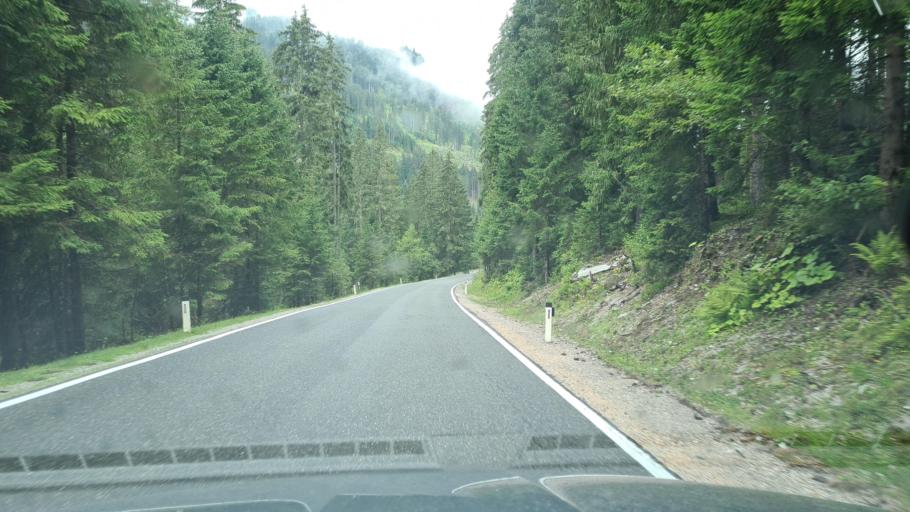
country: AT
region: Salzburg
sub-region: Politischer Bezirk Sankt Johann im Pongau
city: Untertauern
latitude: 47.3033
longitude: 13.4559
